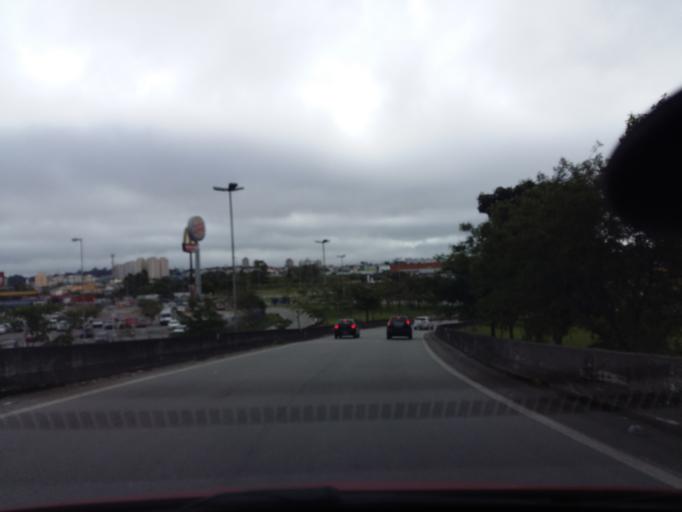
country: BR
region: Sao Paulo
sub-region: Sao Bernardo Do Campo
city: Sao Bernardo do Campo
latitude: -23.6674
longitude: -46.5739
